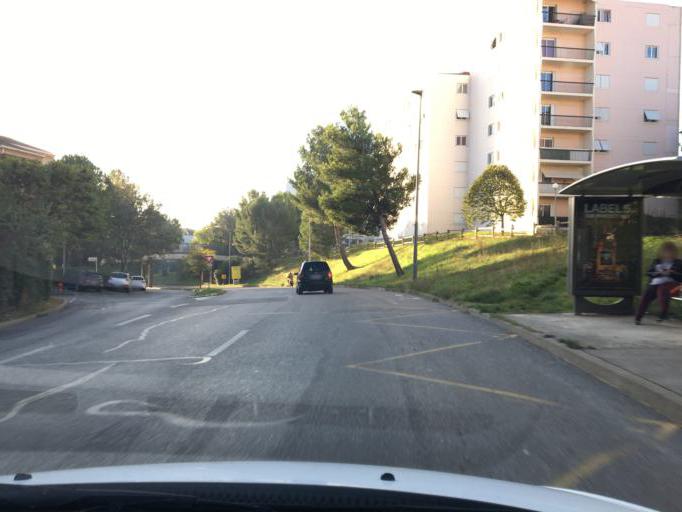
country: FR
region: Provence-Alpes-Cote d'Azur
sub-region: Departement des Bouches-du-Rhone
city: Aix-en-Provence
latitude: 43.5256
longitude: 5.4135
